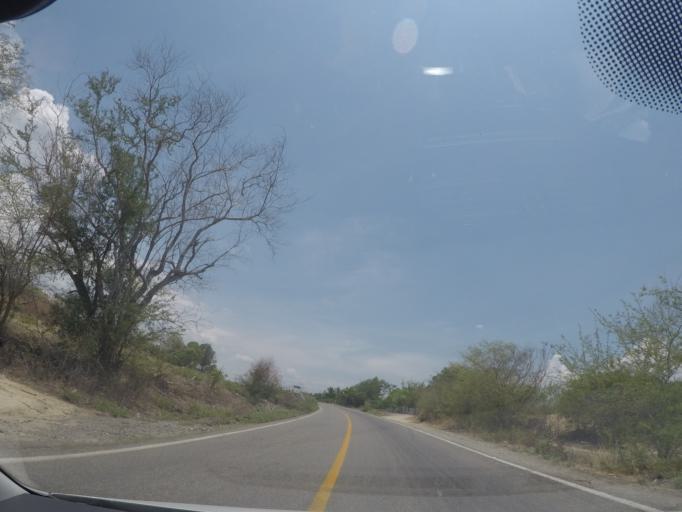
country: MX
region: Oaxaca
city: Santa Maria Jalapa del Marques
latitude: 16.4386
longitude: -95.5229
